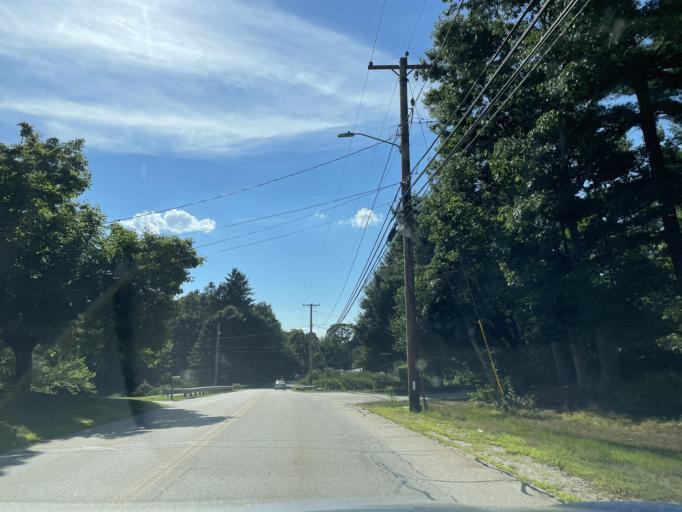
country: US
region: Massachusetts
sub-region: Worcester County
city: Oxford
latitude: 42.1156
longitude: -71.8846
